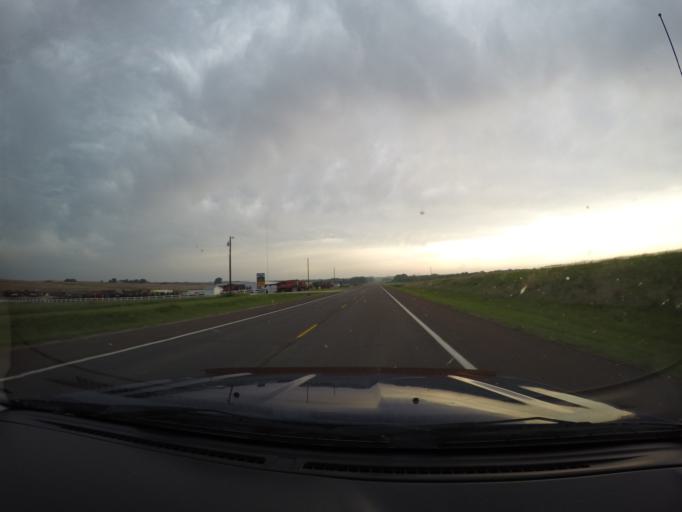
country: US
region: Kansas
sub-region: Clay County
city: Clay Center
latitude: 39.3803
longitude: -97.0526
